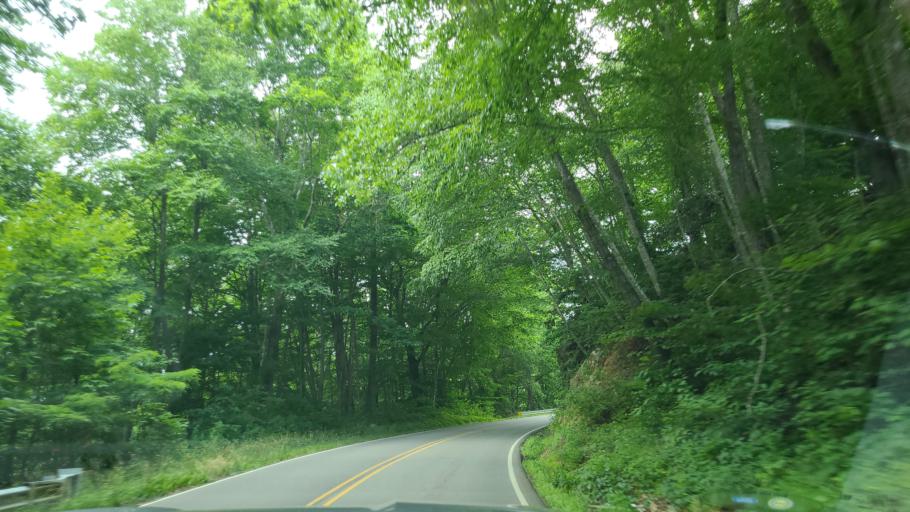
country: US
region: North Carolina
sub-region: Ashe County
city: Jefferson
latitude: 36.3980
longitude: -81.4056
